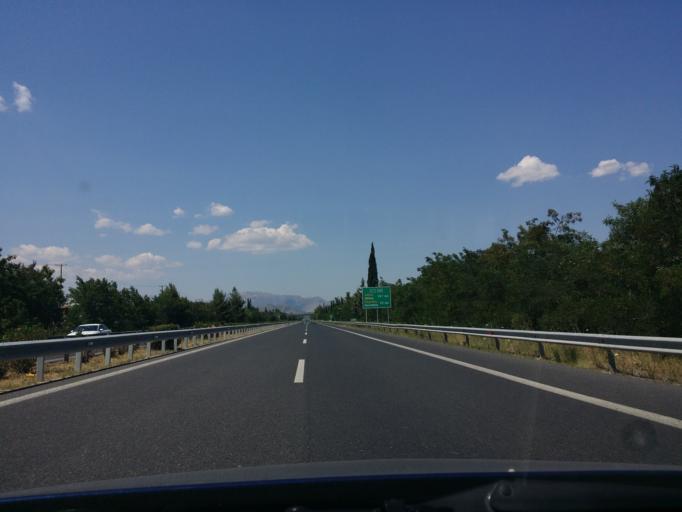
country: GR
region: Peloponnese
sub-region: Nomos Arkadias
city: Tripoli
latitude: 37.5123
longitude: 22.4041
